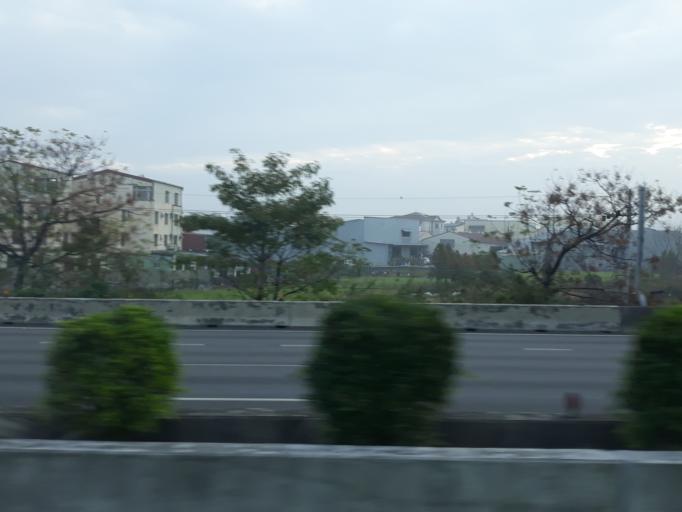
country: TW
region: Taiwan
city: Fengyuan
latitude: 24.2596
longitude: 120.6915
